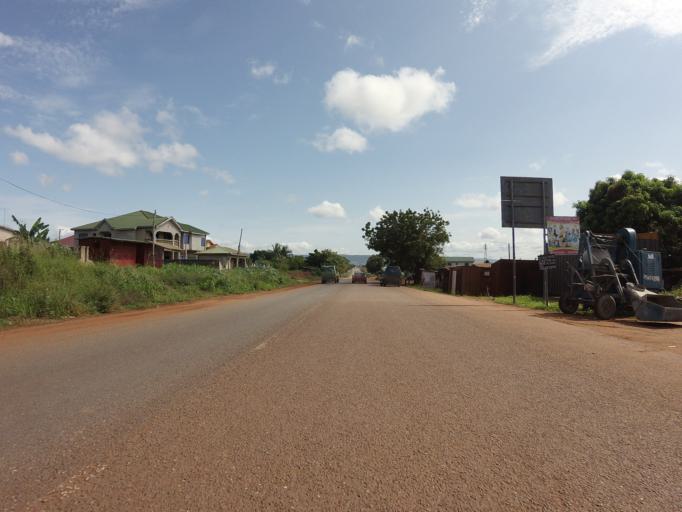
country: GH
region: Eastern
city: Aburi
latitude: 5.8174
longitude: -0.1211
